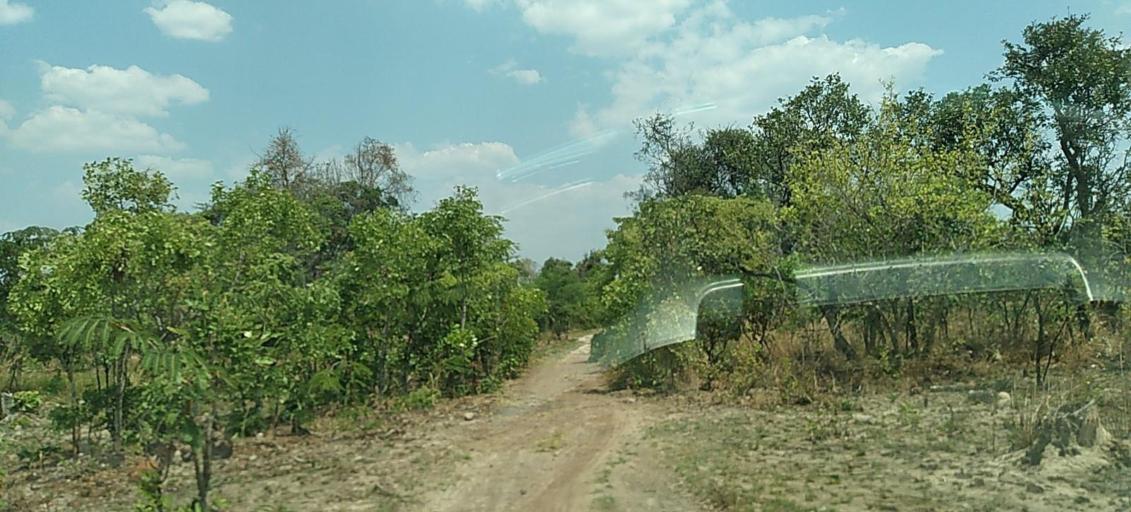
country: CD
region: Katanga
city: Kipushi
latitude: -12.0007
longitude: 27.4234
